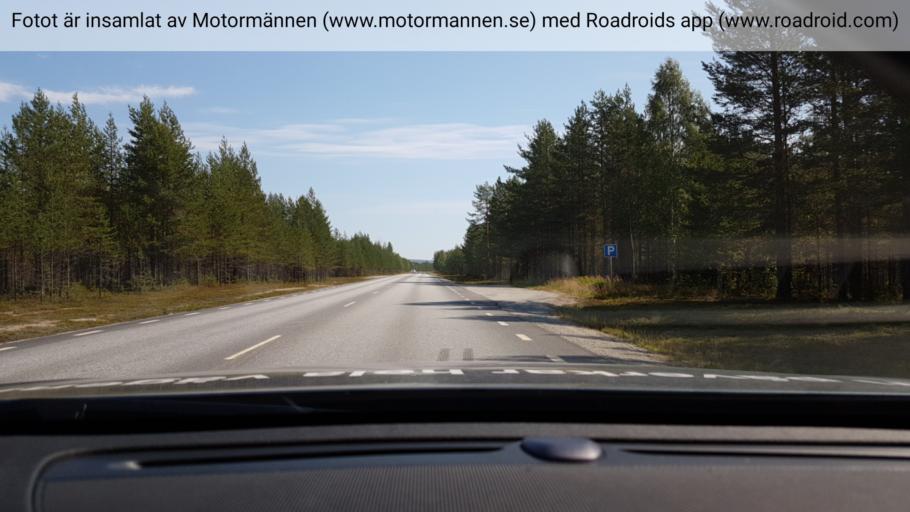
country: SE
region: Vaesterbotten
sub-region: Vindelns Kommun
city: Vindeln
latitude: 64.1624
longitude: 19.8185
